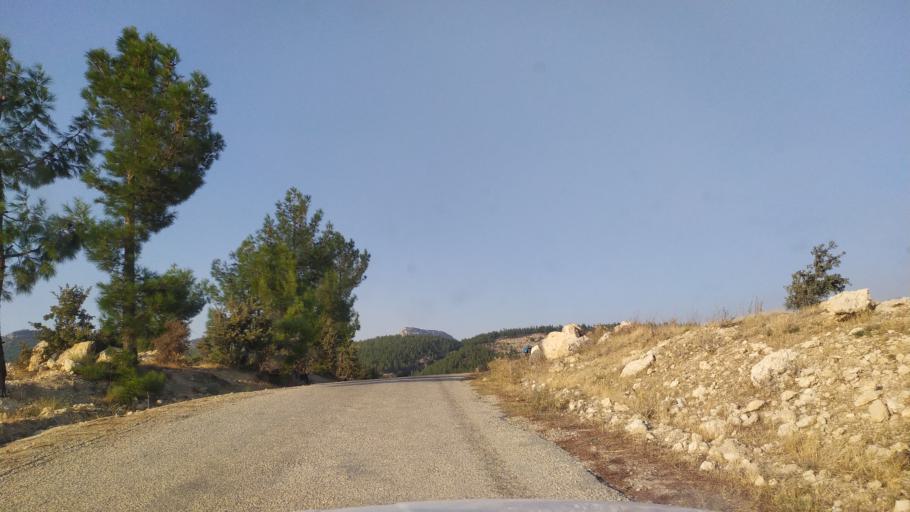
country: TR
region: Mersin
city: Mut
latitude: 36.6896
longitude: 33.1979
